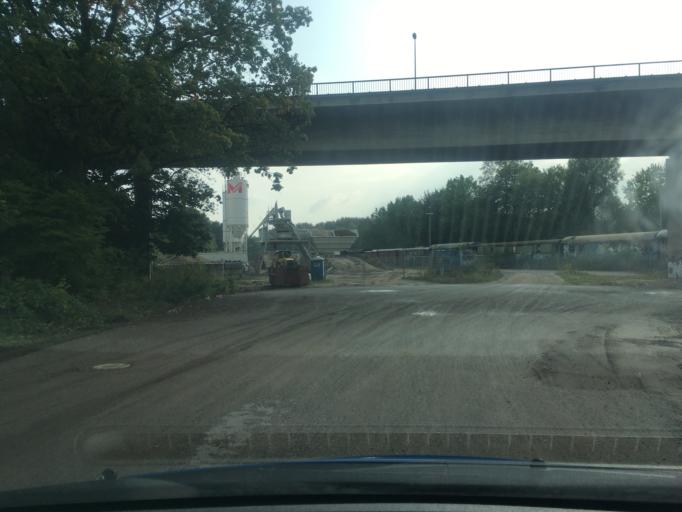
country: DE
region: Lower Saxony
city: Lueneburg
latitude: 53.2395
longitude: 10.4198
